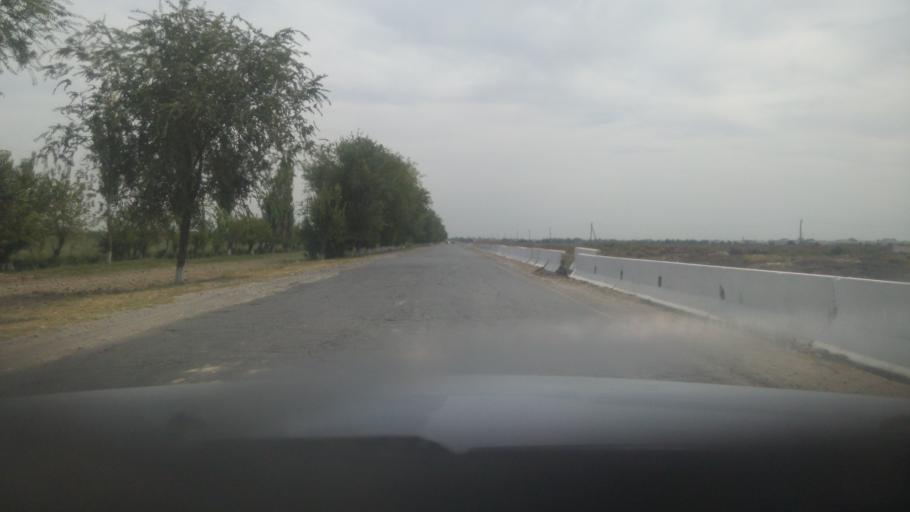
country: UZ
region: Sirdaryo
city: Guliston
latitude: 40.5160
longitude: 68.7937
